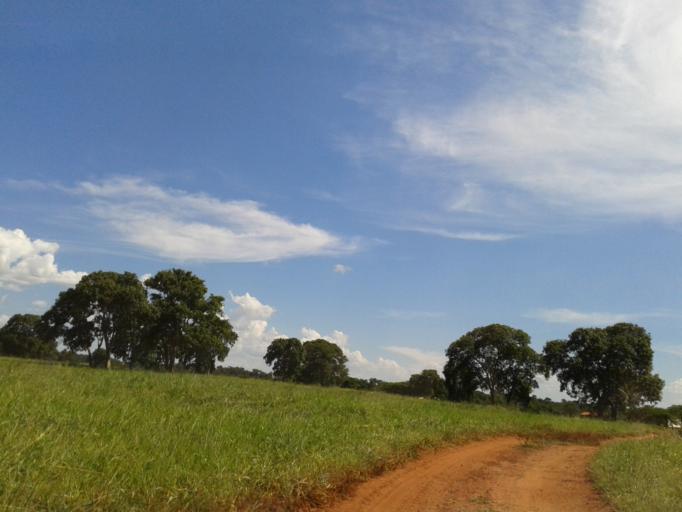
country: BR
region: Minas Gerais
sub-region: Santa Vitoria
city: Santa Vitoria
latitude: -19.1359
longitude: -50.5443
